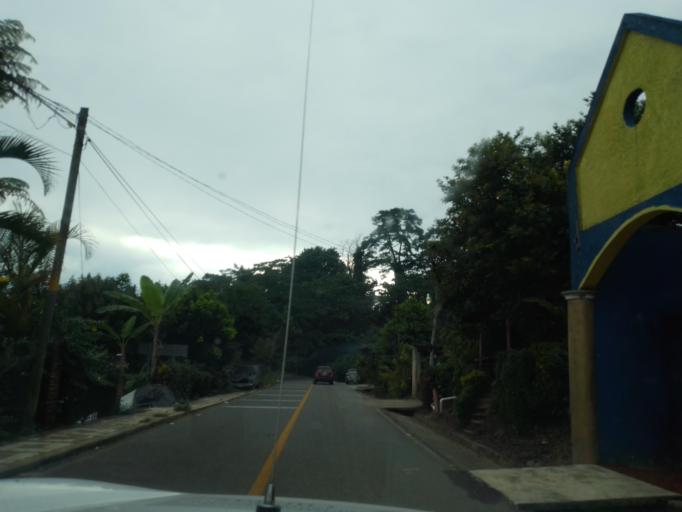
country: MX
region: Chiapas
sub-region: Union Juarez
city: Santo Domingo
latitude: 15.0372
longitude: -92.1201
